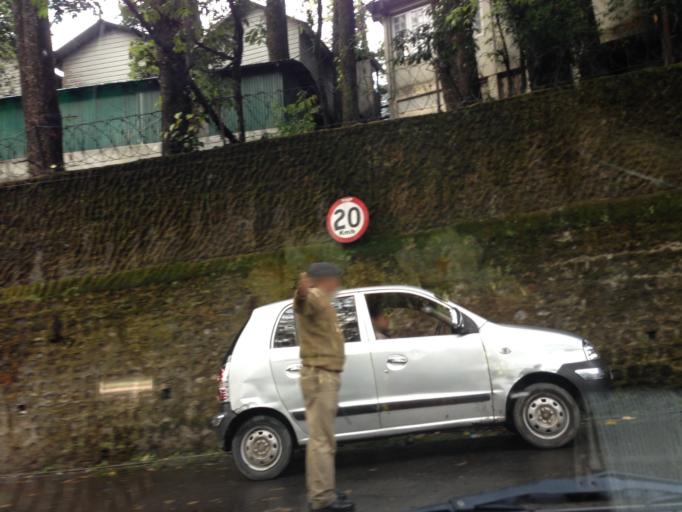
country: IN
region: West Bengal
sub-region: Darjiling
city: Darjiling
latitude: 27.0562
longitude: 88.2558
